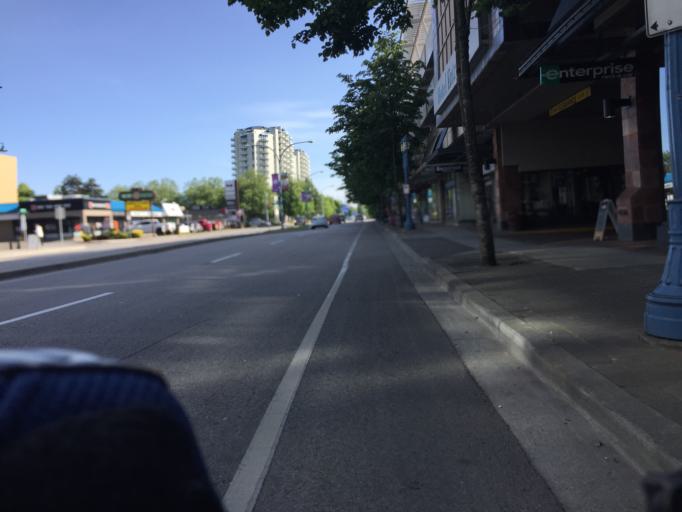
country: CA
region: British Columbia
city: Richmond
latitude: 49.1717
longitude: -123.1403
